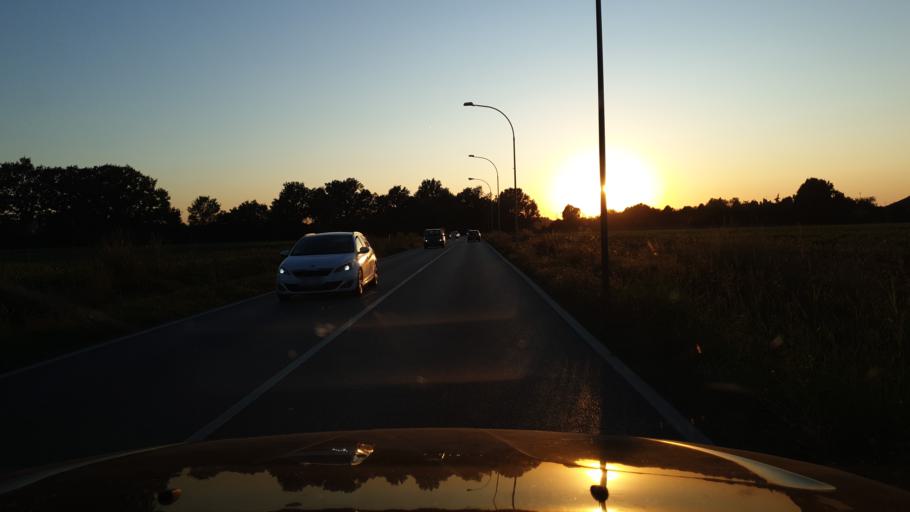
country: IT
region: Emilia-Romagna
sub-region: Provincia di Bologna
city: Quarto Inferiore
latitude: 44.5272
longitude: 11.3936
